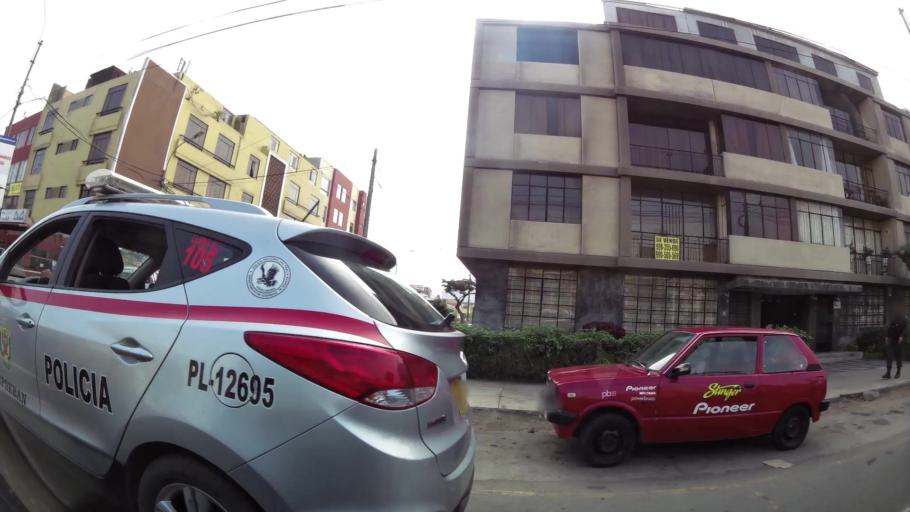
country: PE
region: Lima
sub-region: Lima
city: San Isidro
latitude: -12.0834
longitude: -77.0607
